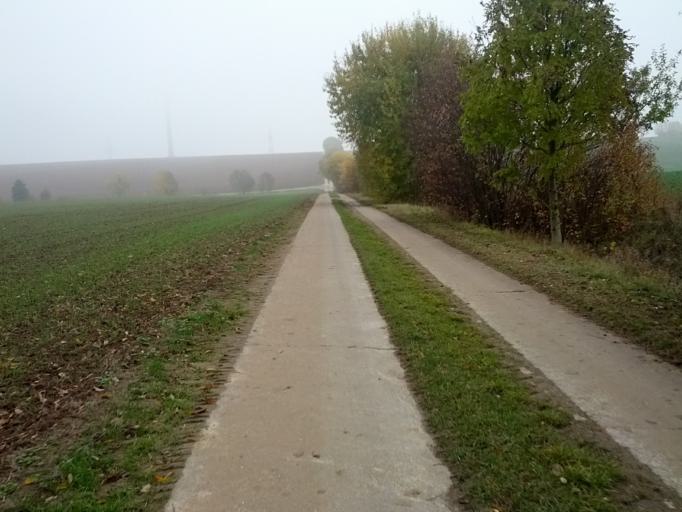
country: DE
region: Thuringia
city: Bischofroda
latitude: 51.0057
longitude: 10.3736
